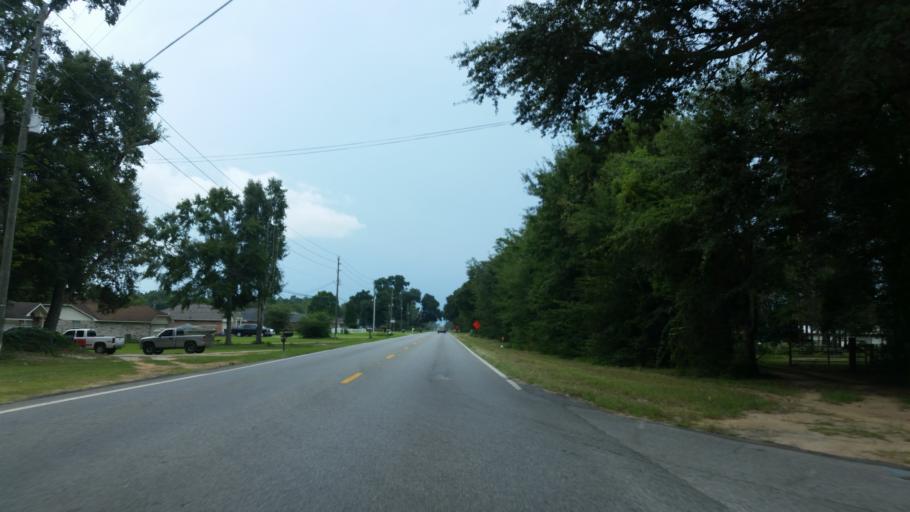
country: US
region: Florida
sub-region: Santa Rosa County
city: Pace
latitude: 30.6258
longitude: -87.1649
